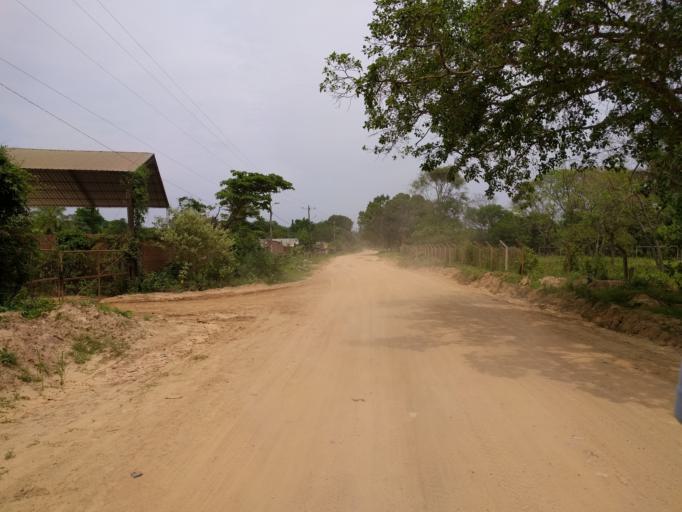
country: BO
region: Santa Cruz
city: Santa Rita
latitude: -17.9422
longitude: -63.3598
